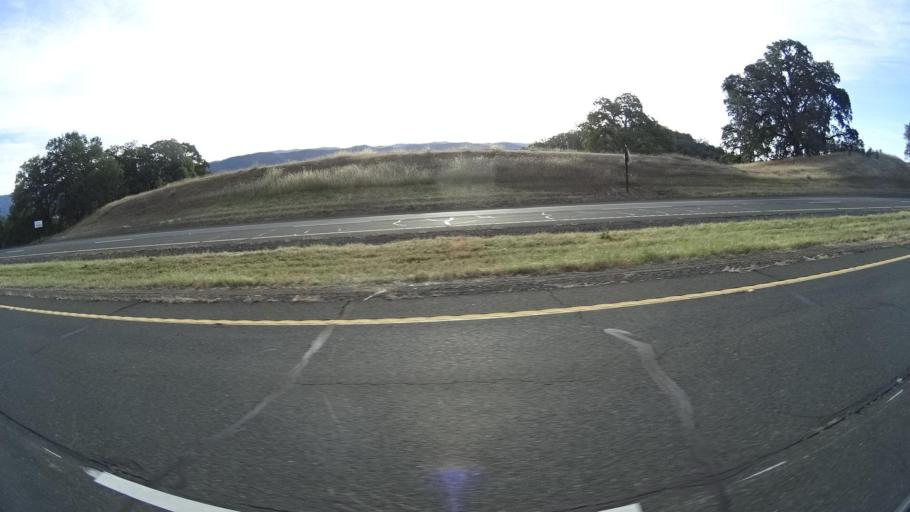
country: US
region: California
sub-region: Lake County
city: North Lakeport
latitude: 39.1240
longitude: -122.9065
